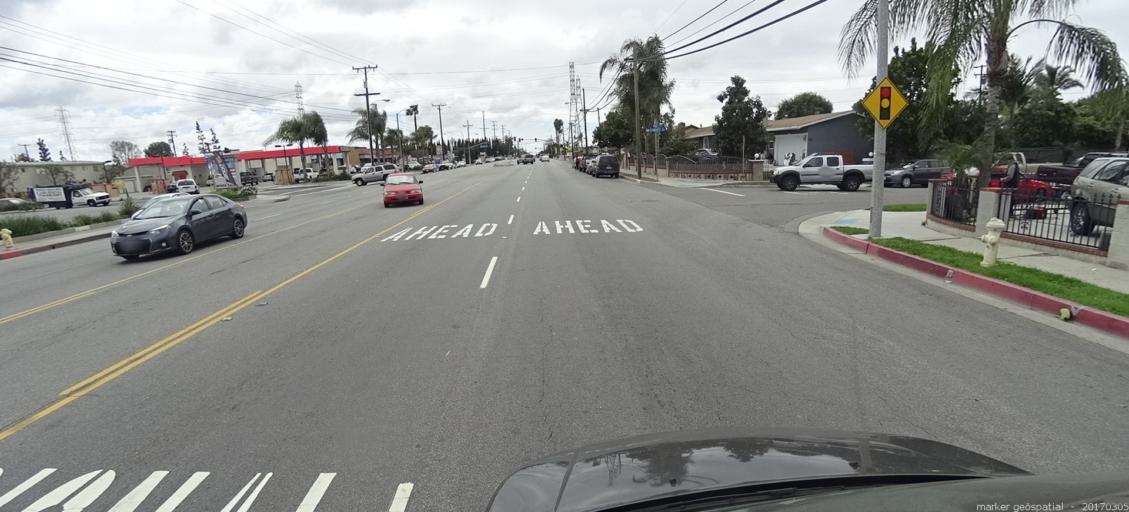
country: US
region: California
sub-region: Orange County
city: Stanton
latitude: 33.8093
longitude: -117.9758
